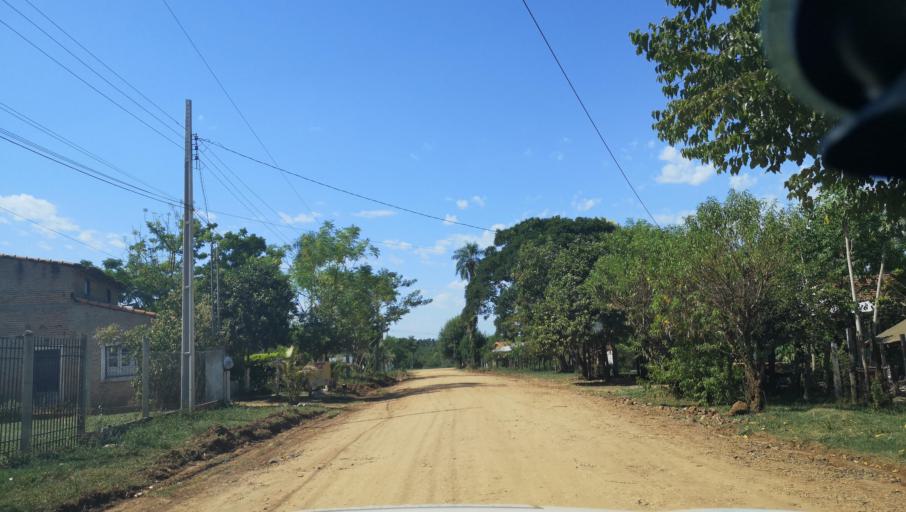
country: PY
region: Itapua
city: Carmen del Parana
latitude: -27.1728
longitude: -56.2331
